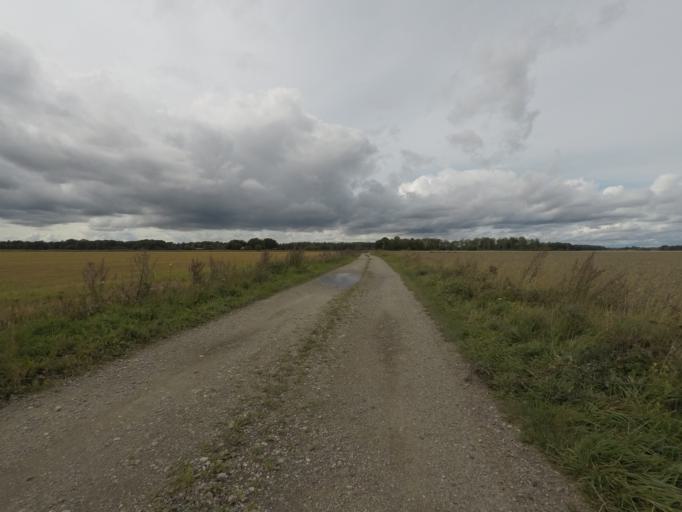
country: SE
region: Vaestmanland
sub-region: Kungsors Kommun
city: Kungsoer
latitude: 59.4546
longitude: 16.0702
